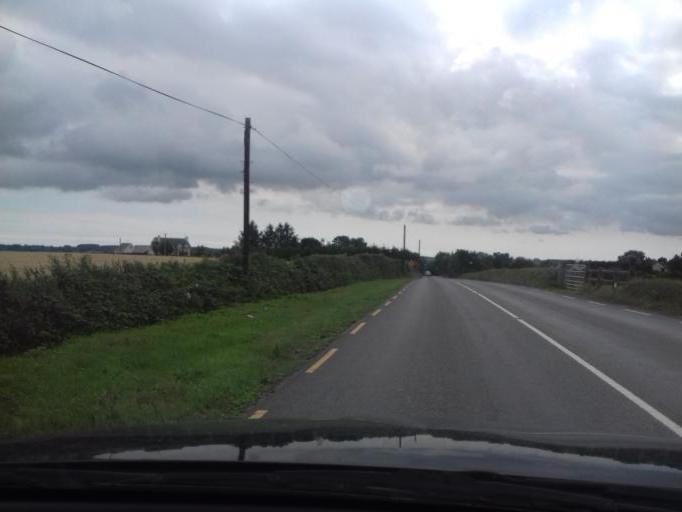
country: IE
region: Leinster
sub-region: Loch Garman
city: Ballinroad
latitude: 52.4705
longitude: -6.3997
